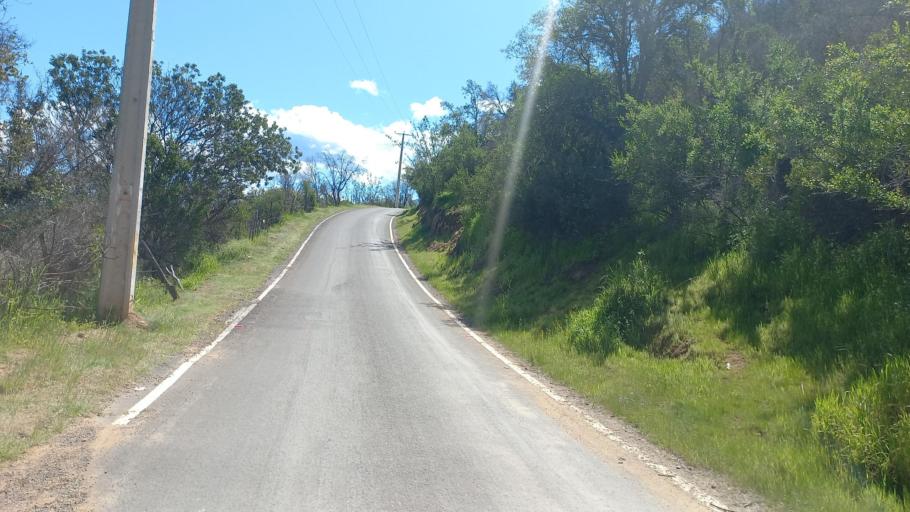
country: CL
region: Santiago Metropolitan
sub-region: Provincia de Chacabuco
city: Lampa
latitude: -33.1945
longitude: -71.0908
